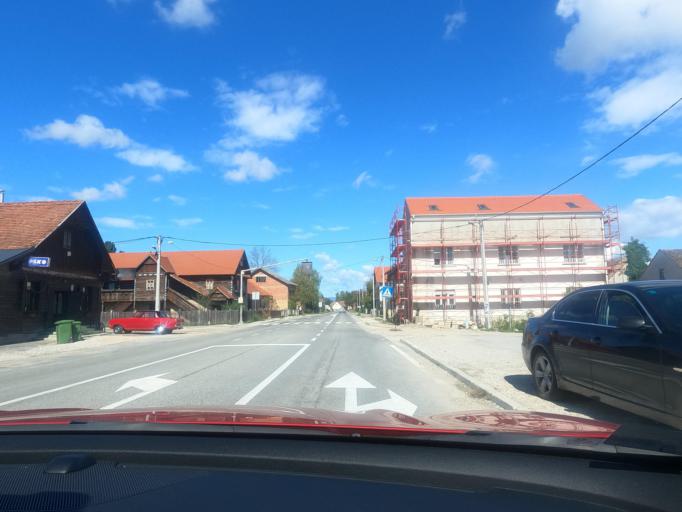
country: HR
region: Zagrebacka
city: Turopolje
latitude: 45.6338
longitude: 16.1159
